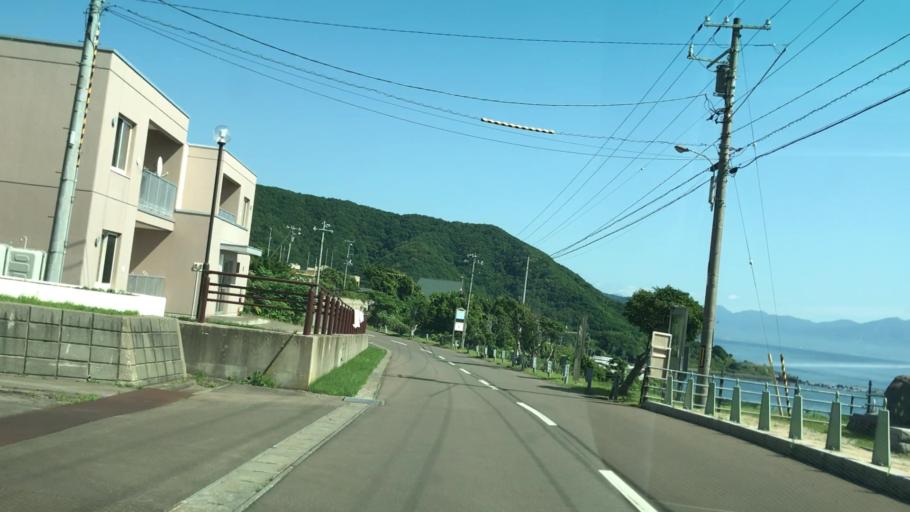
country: JP
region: Hokkaido
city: Iwanai
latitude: 43.1472
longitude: 140.4216
